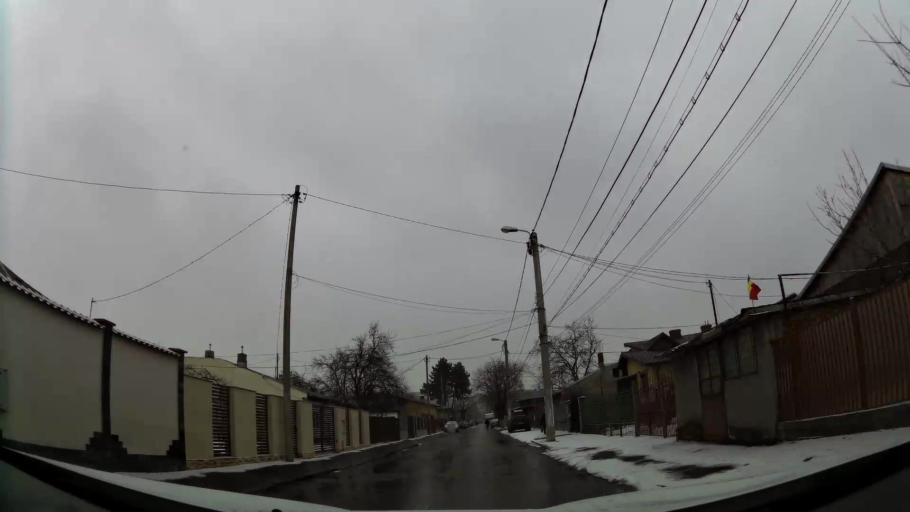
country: RO
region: Prahova
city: Ploiesti
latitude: 44.9461
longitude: 26.0015
